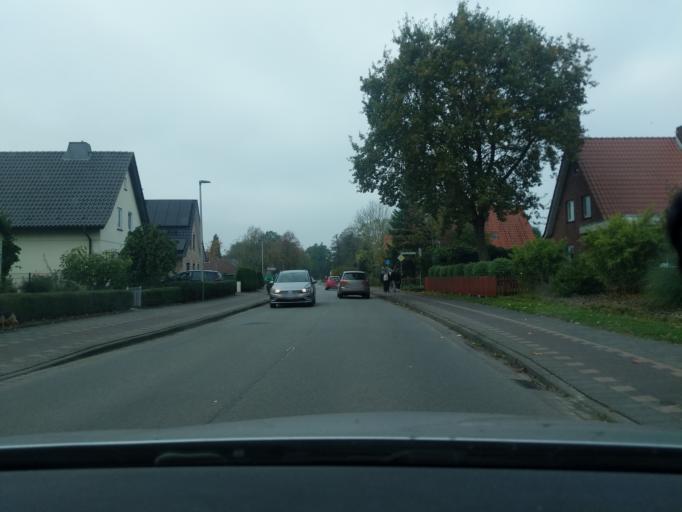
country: DE
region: Lower Saxony
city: Otterndorf
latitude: 53.8124
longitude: 8.8908
